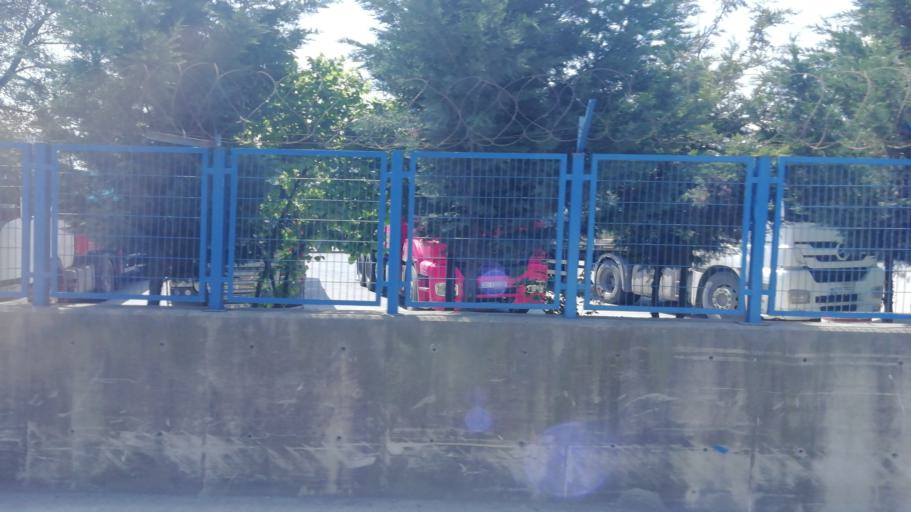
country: TR
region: Kocaeli
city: Gebze
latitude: 40.7972
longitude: 29.4527
